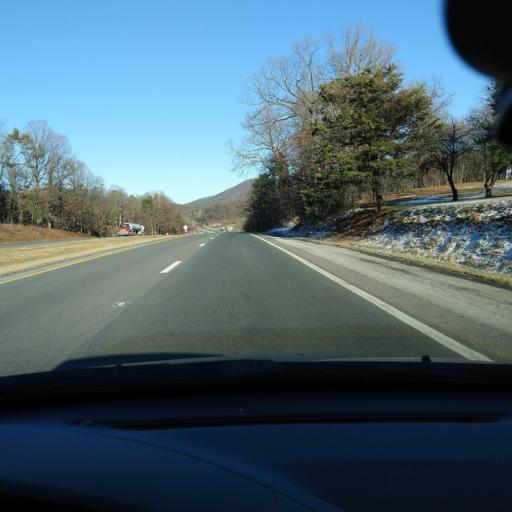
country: US
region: Virginia
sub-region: Botetourt County
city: Blue Ridge
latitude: 37.3616
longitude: -79.8256
